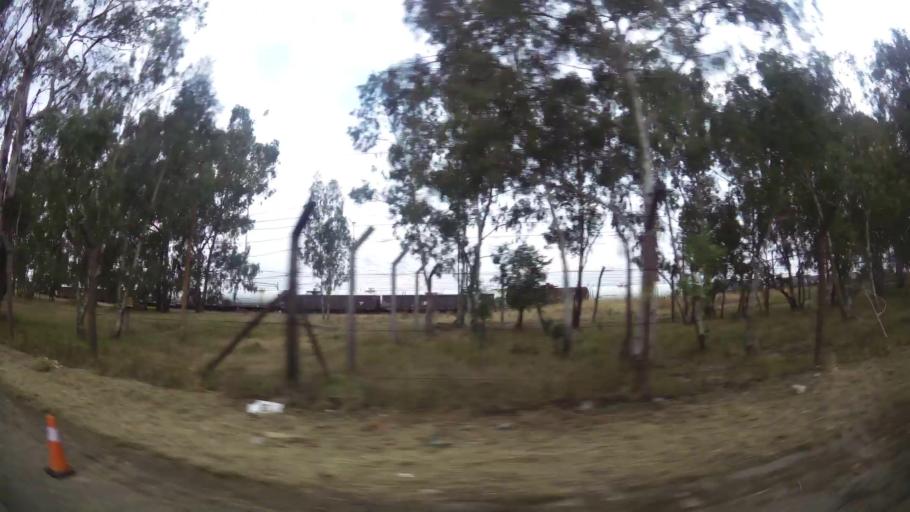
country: ZA
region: Orange Free State
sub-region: Fezile Dabi District Municipality
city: Sasolburg
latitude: -26.8495
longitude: 27.8679
